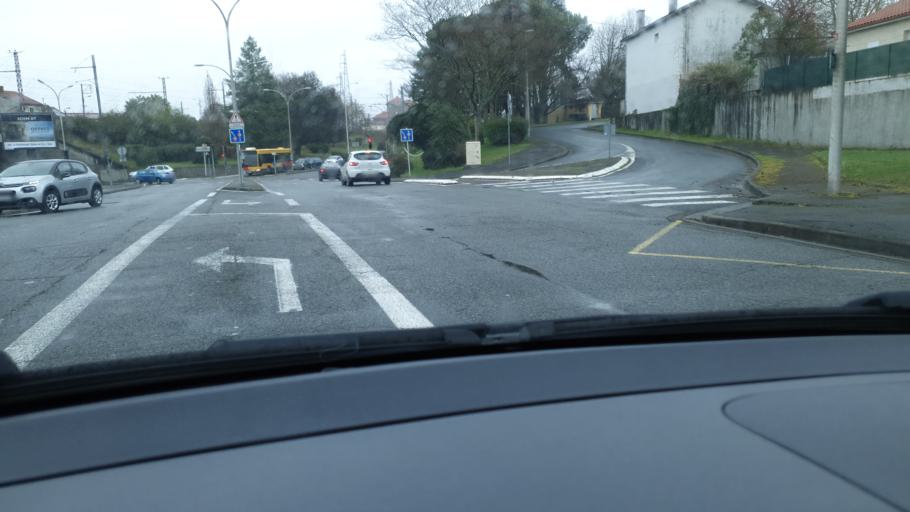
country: FR
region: Midi-Pyrenees
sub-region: Departement des Hautes-Pyrenees
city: Tarbes
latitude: 43.2405
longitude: 0.0577
